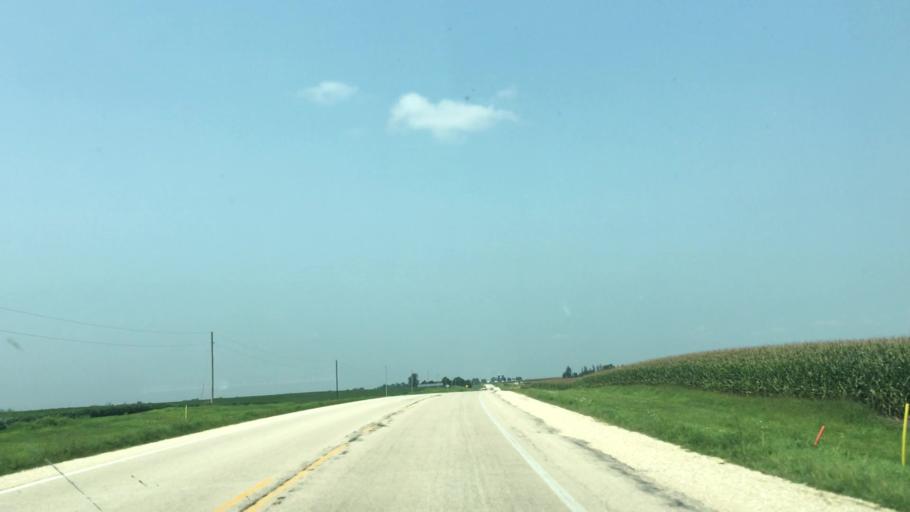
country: US
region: Iowa
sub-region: Fayette County
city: West Union
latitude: 42.9825
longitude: -91.8243
